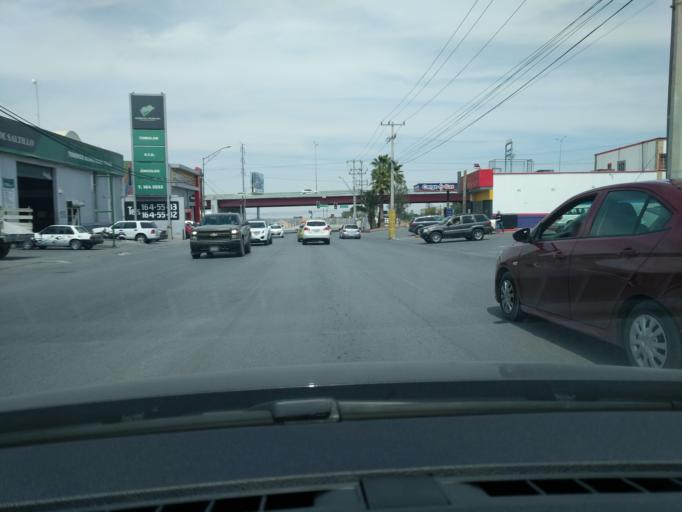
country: MX
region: Coahuila
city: Saltillo
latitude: 25.4294
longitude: -100.9469
